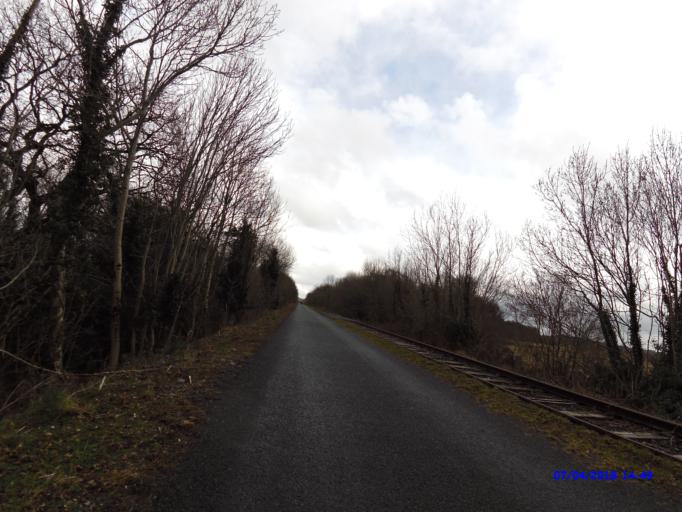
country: IE
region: Leinster
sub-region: An Iarmhi
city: Athlone
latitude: 53.4158
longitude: -7.8627
